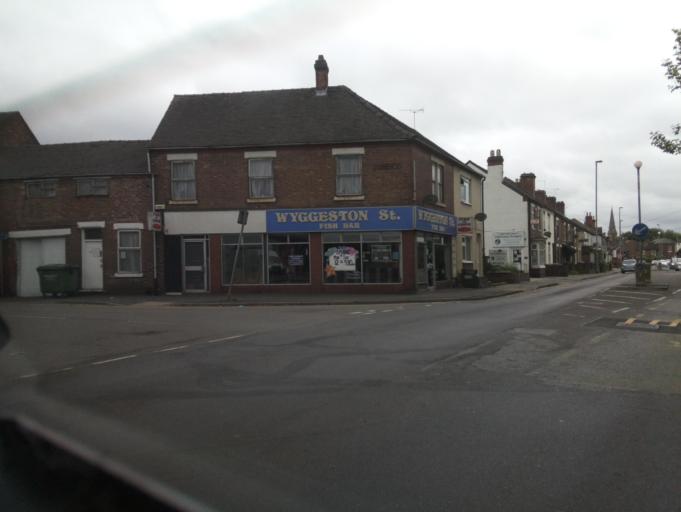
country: GB
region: England
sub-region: Staffordshire
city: Burton upon Trent
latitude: 52.8201
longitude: -1.6404
